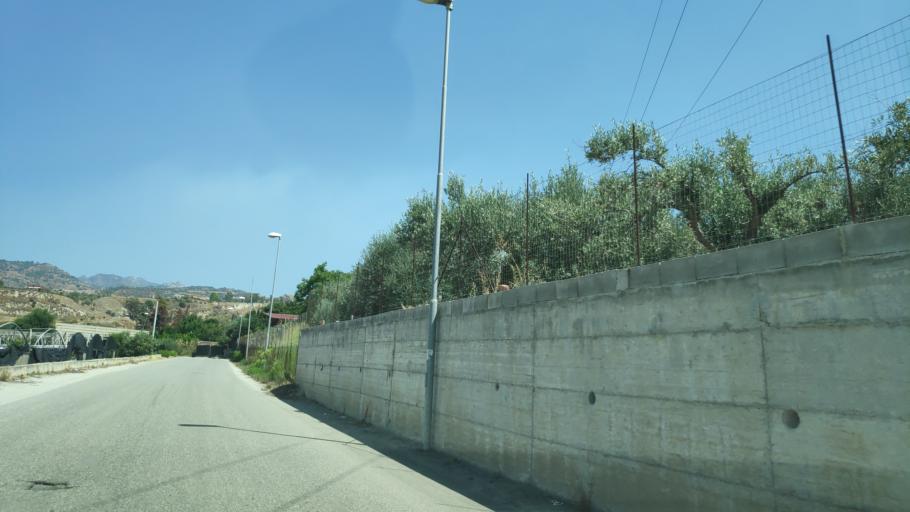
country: IT
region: Calabria
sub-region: Provincia di Reggio Calabria
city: Bova Marina
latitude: 37.9336
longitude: 15.9114
